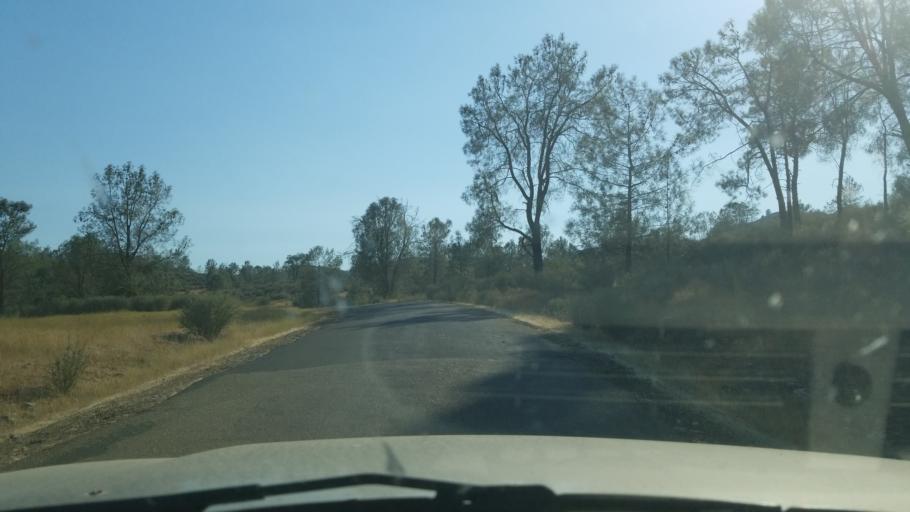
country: US
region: California
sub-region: Tuolumne County
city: Jamestown
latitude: 37.8475
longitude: -120.4611
